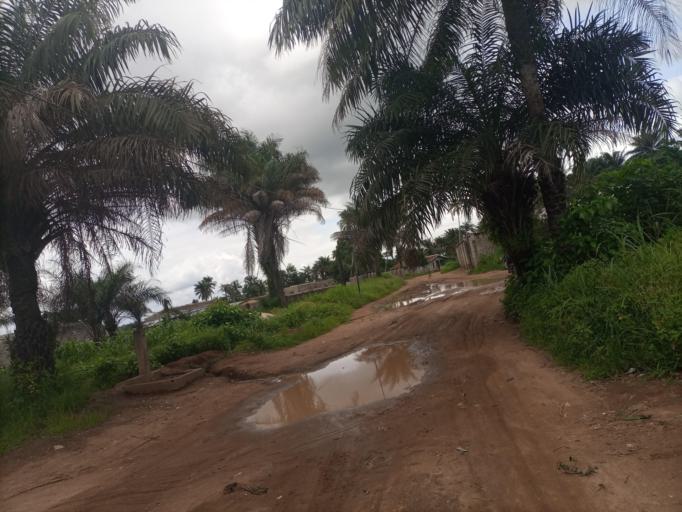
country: SL
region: Northern Province
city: Masoyila
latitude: 8.5946
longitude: -13.1636
